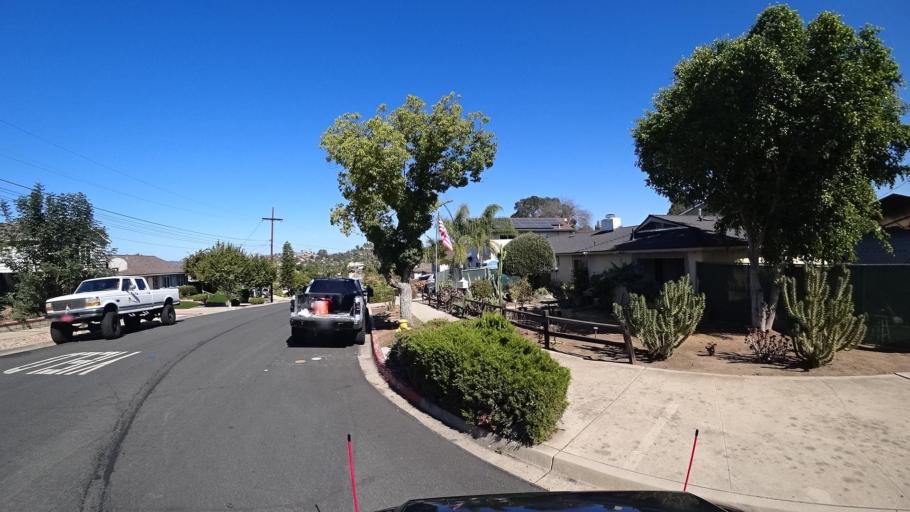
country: US
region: California
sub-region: San Diego County
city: Bostonia
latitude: 32.8176
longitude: -116.9228
